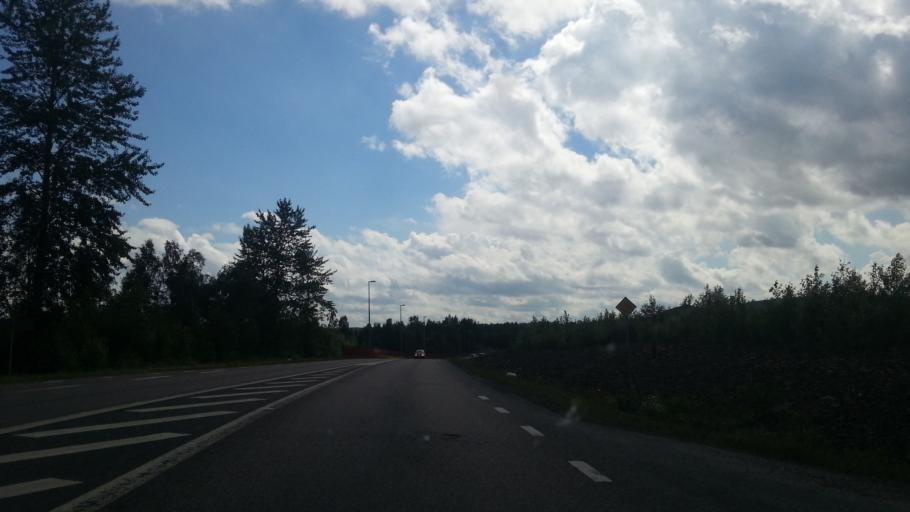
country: SE
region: Dalarna
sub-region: Faluns Kommun
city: Falun
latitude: 60.6111
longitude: 15.6163
